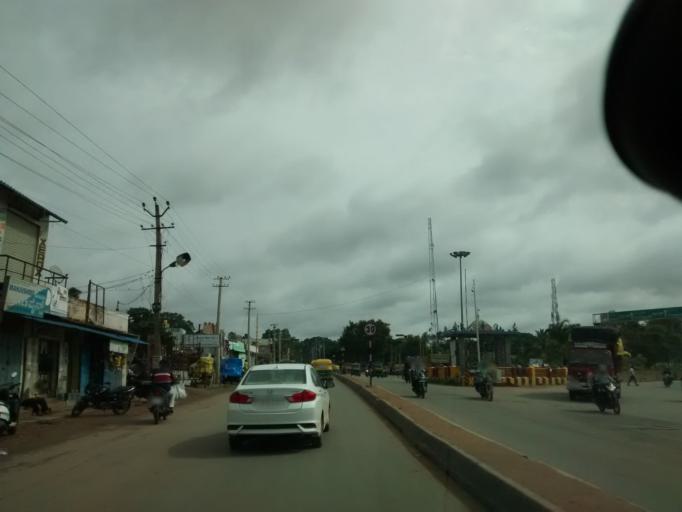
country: IN
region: Karnataka
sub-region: Tumkur
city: Tumkur
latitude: 13.3620
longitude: 77.1032
